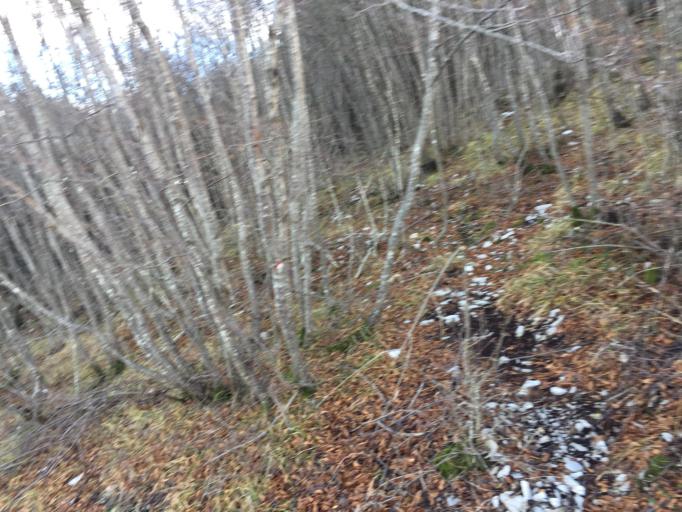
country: IT
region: Friuli Venezia Giulia
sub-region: Provincia di Trieste
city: Dolina
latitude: 45.6462
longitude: 13.8918
